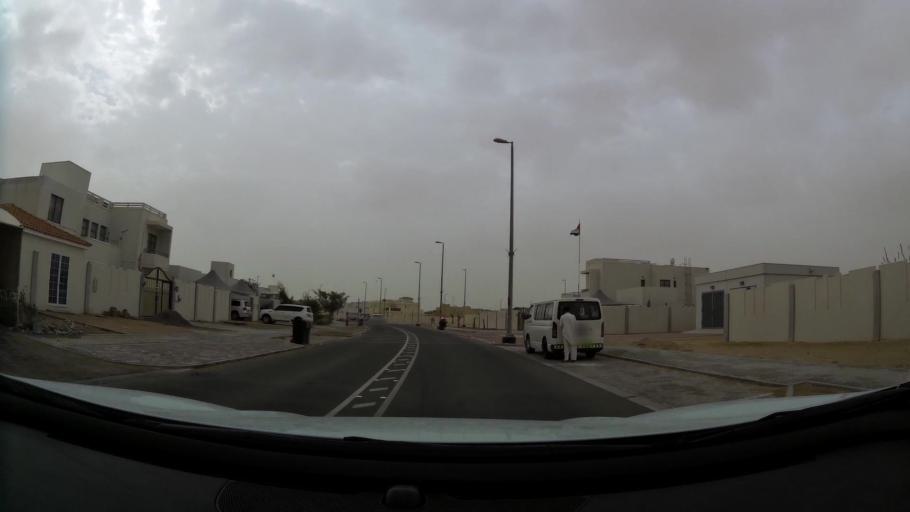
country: AE
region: Abu Dhabi
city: Abu Dhabi
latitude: 24.4529
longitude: 54.7217
